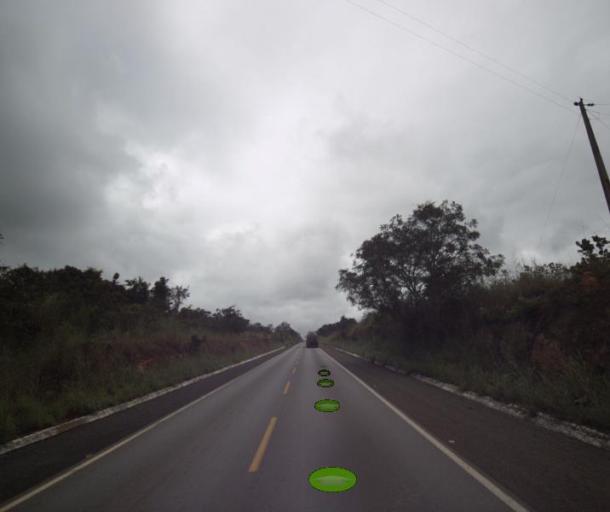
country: BR
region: Goias
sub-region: Uruacu
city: Uruacu
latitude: -14.7514
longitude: -49.0673
